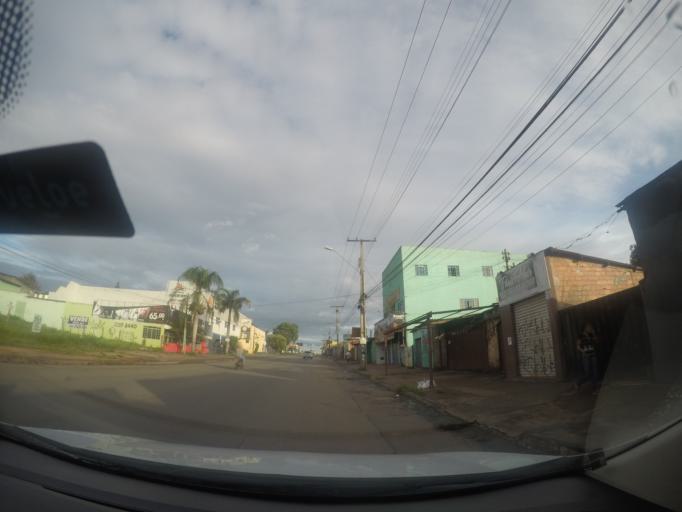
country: BR
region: Goias
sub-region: Goiania
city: Goiania
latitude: -16.6570
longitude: -49.3285
